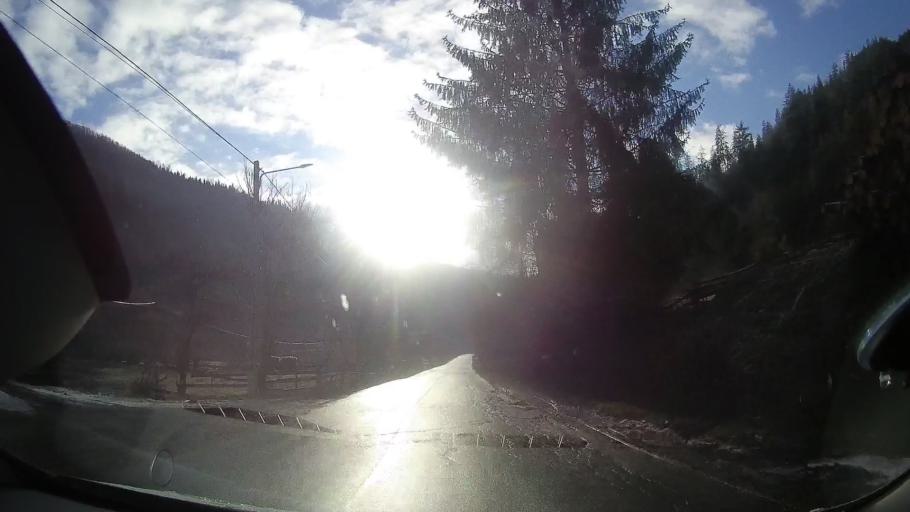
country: RO
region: Alba
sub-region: Comuna Albac
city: Albac
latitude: 46.4426
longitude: 22.9663
